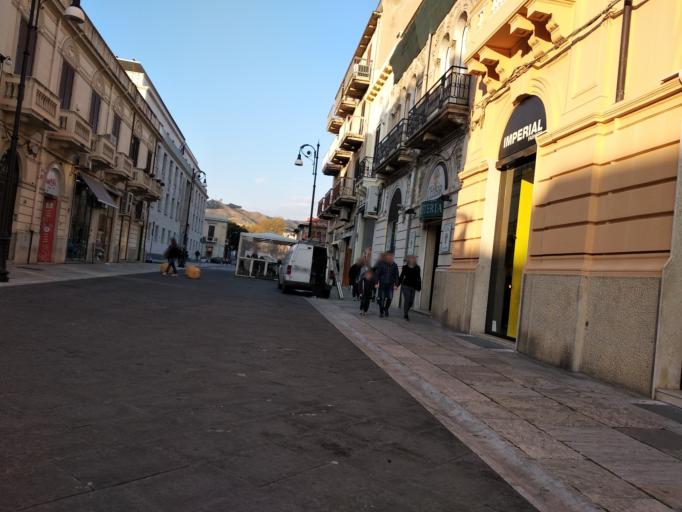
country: IT
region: Calabria
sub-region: Provincia di Reggio Calabria
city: Reggio Calabria
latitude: 38.1140
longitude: 15.6507
